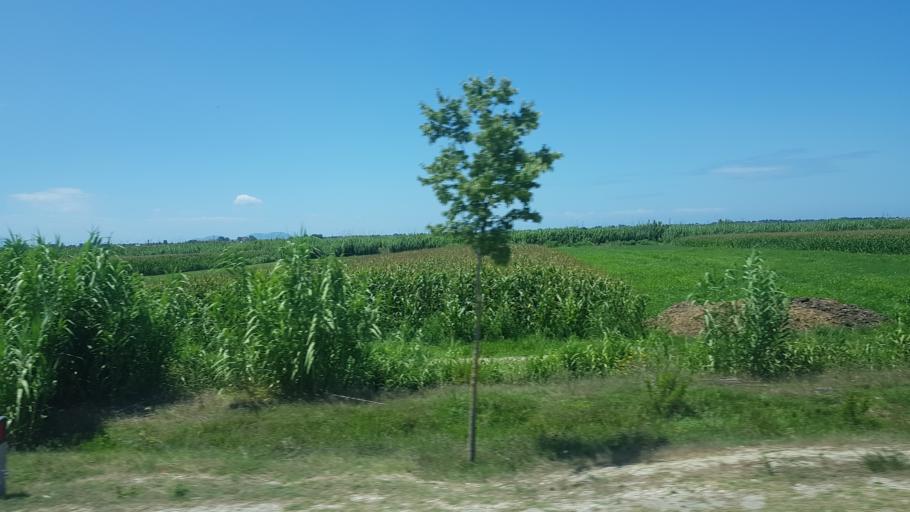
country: AL
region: Fier
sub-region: Rrethi i Fierit
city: Frakulla e Madhe
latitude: 40.6522
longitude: 19.4939
